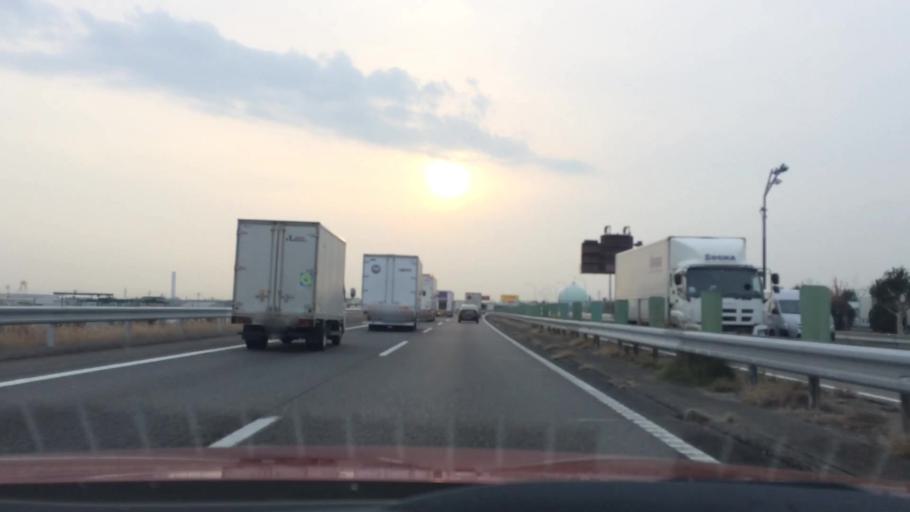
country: JP
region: Aichi
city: Iwakura
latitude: 35.2777
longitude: 136.8477
